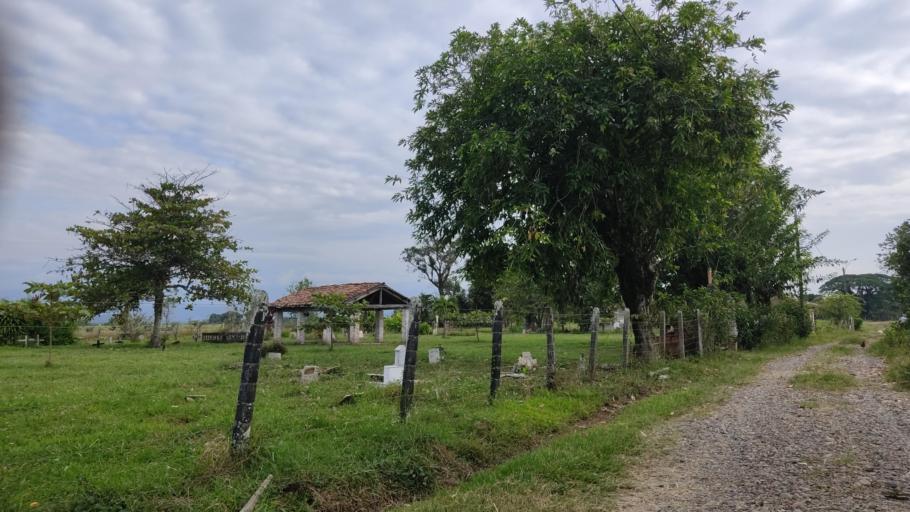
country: CO
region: Valle del Cauca
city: Jamundi
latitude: 3.1319
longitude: -76.5595
